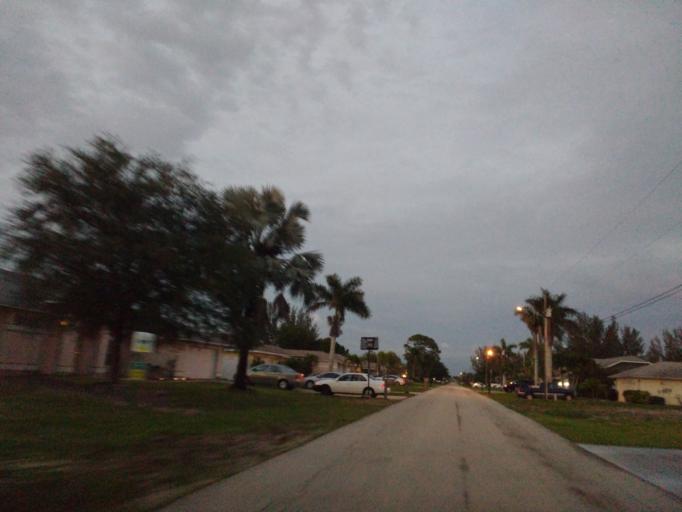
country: US
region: Florida
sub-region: Lee County
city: Cape Coral
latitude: 26.6152
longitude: -81.9728
